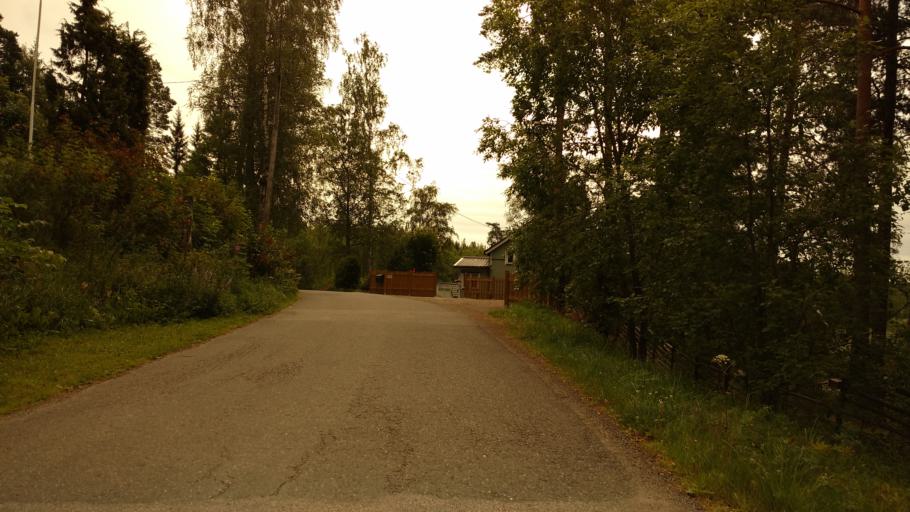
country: FI
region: Varsinais-Suomi
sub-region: Turku
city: Lieto
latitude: 60.4388
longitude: 22.4413
